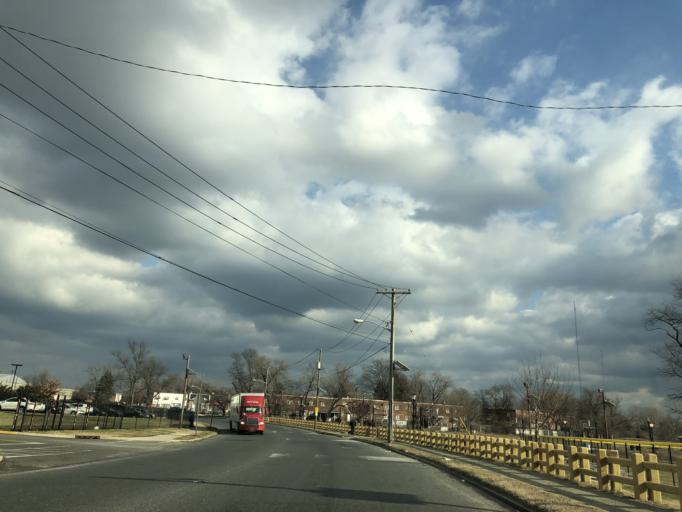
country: US
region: New Jersey
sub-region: Camden County
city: Wood-Lynne
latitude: 39.9126
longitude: -75.1099
